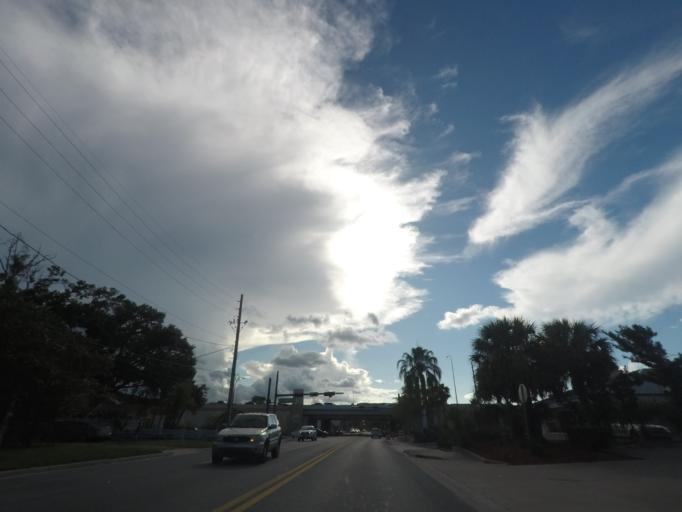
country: US
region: Florida
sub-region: Orange County
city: Fairview Shores
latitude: 28.5823
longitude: -81.3738
